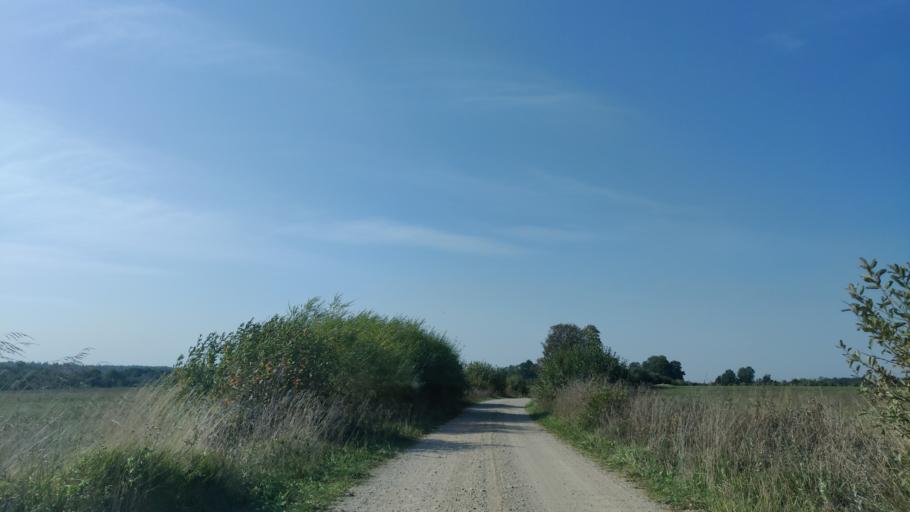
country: LT
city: Sirvintos
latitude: 54.9666
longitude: 24.7998
